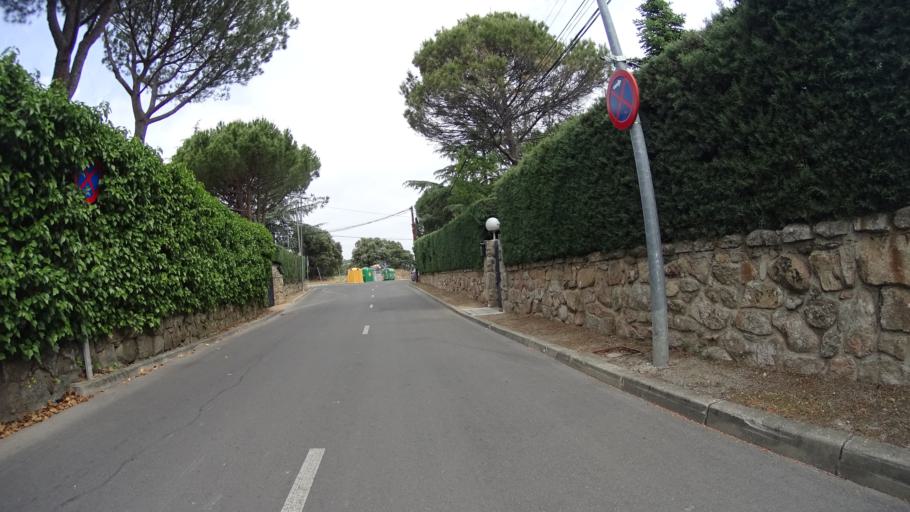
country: ES
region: Madrid
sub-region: Provincia de Madrid
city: Galapagar
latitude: 40.5699
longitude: -4.0014
